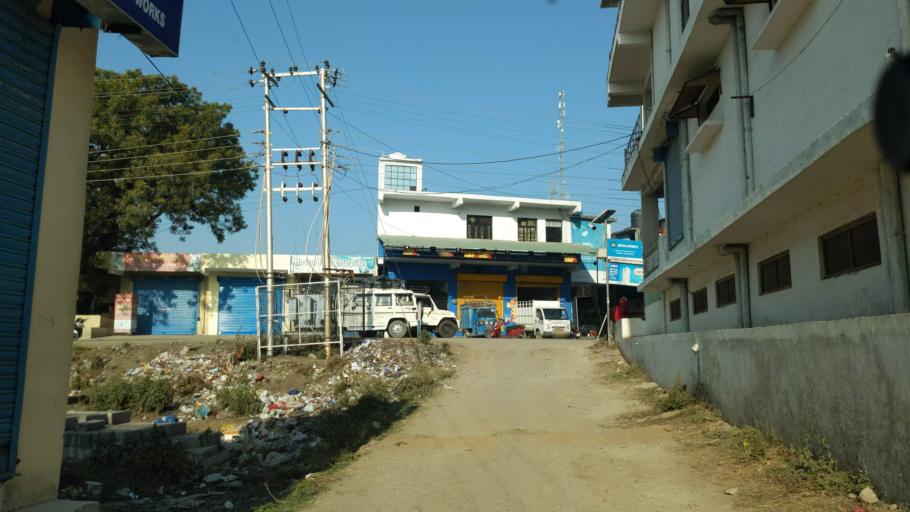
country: IN
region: Uttarakhand
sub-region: Naini Tal
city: Haldwani
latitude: 29.2078
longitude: 79.4949
